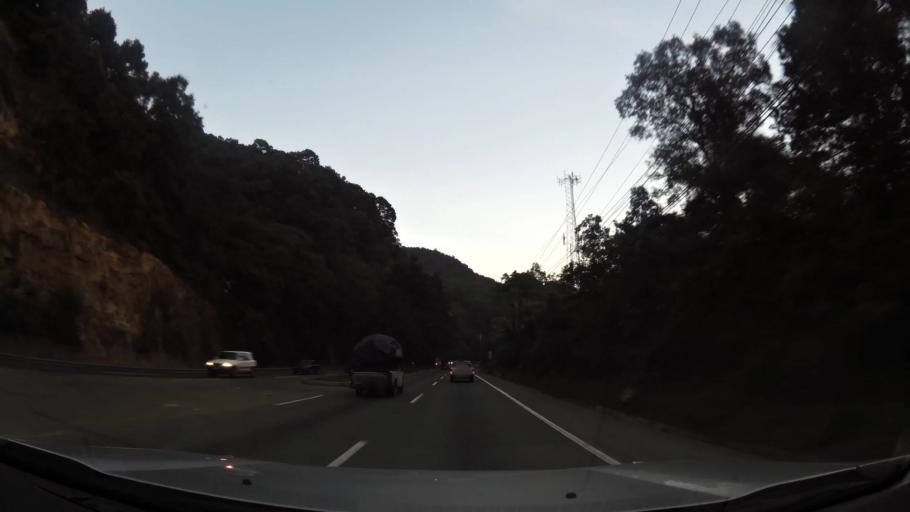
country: GT
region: Sacatepequez
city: San Lucas Sacatepequez
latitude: 14.6051
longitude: -90.6349
